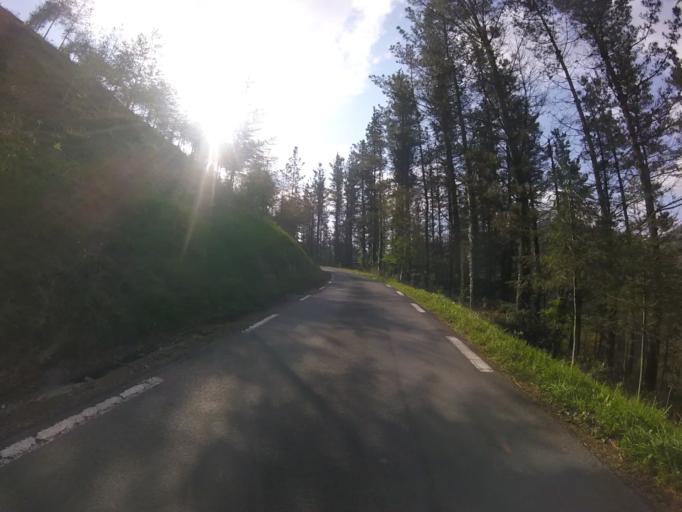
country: ES
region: Basque Country
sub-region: Provincia de Guipuzcoa
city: Azkoitia
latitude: 43.2241
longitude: -2.3165
